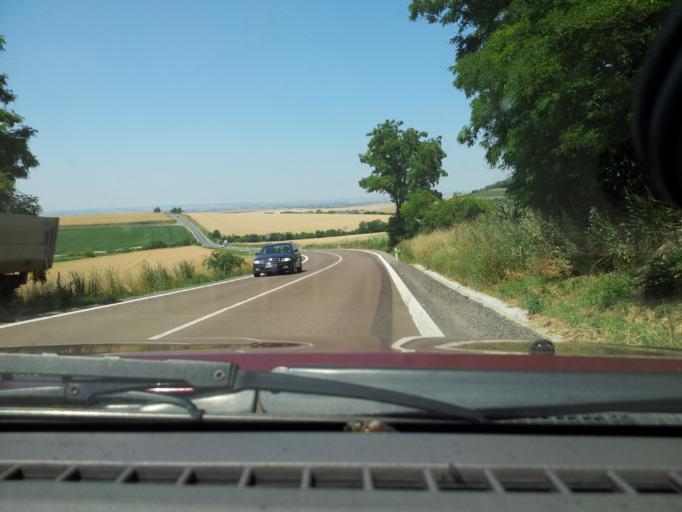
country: CZ
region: South Moravian
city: Sitborice
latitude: 49.0317
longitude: 16.7958
